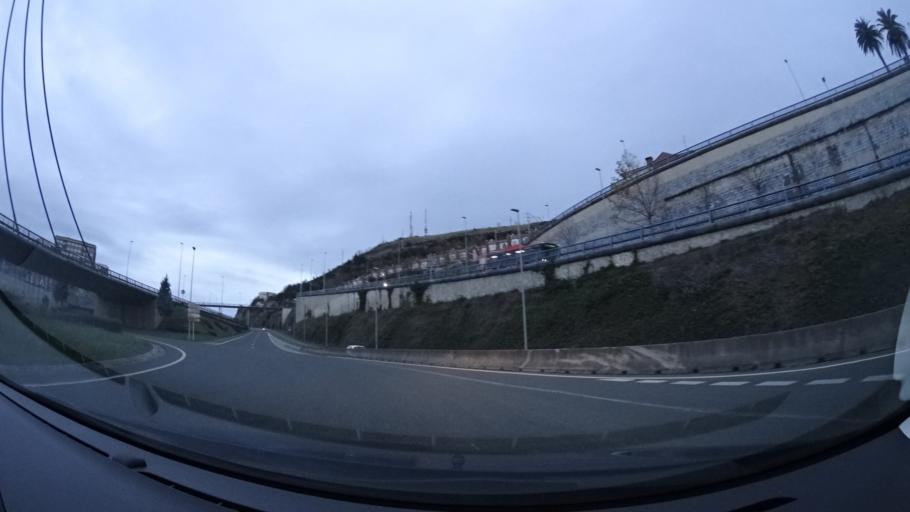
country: ES
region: Basque Country
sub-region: Bizkaia
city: Bilbao
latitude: 43.2741
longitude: -2.9537
